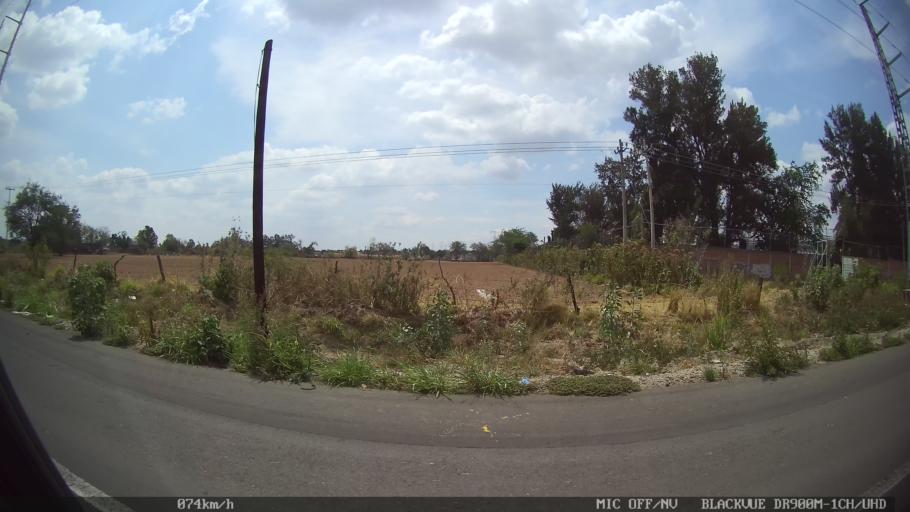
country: MX
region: Jalisco
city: Tonala
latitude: 20.6455
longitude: -103.2363
